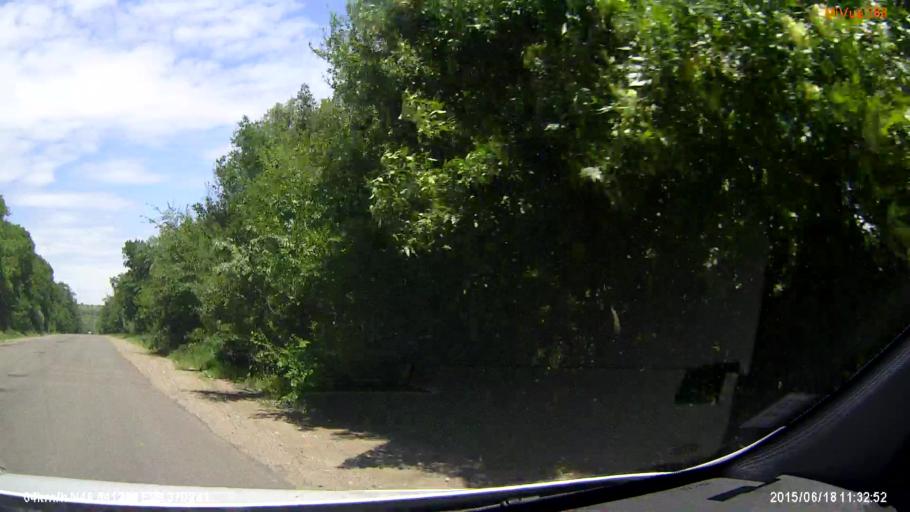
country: MD
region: Causeni
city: Causeni
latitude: 46.6411
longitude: 29.3702
